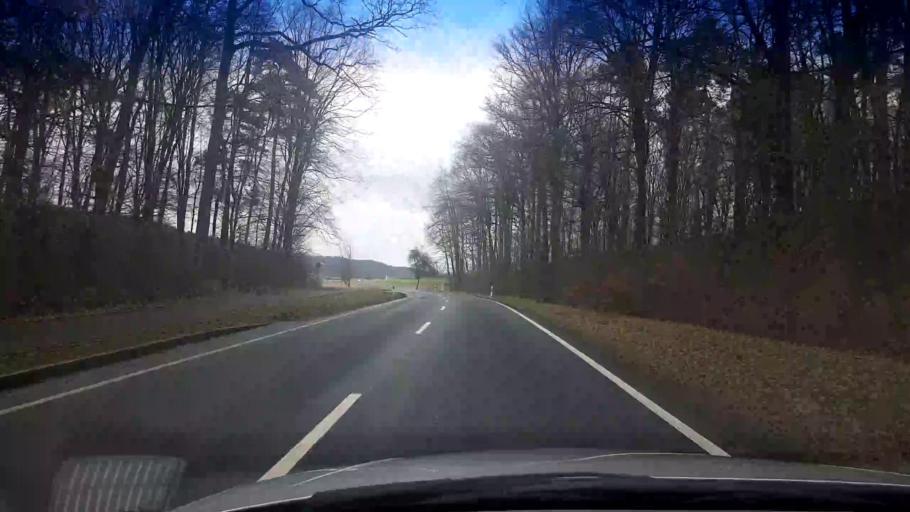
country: DE
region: Bavaria
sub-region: Regierungsbezirk Unterfranken
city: Sand
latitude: 49.9554
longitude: 10.5801
